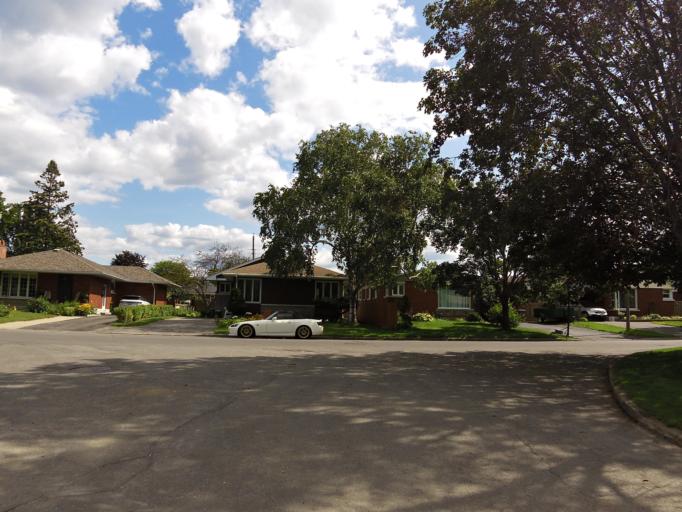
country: CA
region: Ontario
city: Bells Corners
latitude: 45.3655
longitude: -75.7673
